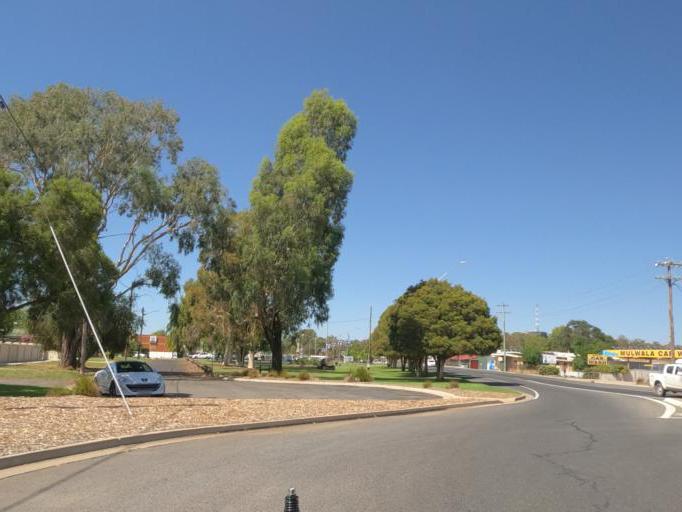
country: AU
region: New South Wales
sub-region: Corowa Shire
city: Mulwala
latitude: -35.9924
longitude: 146.0025
